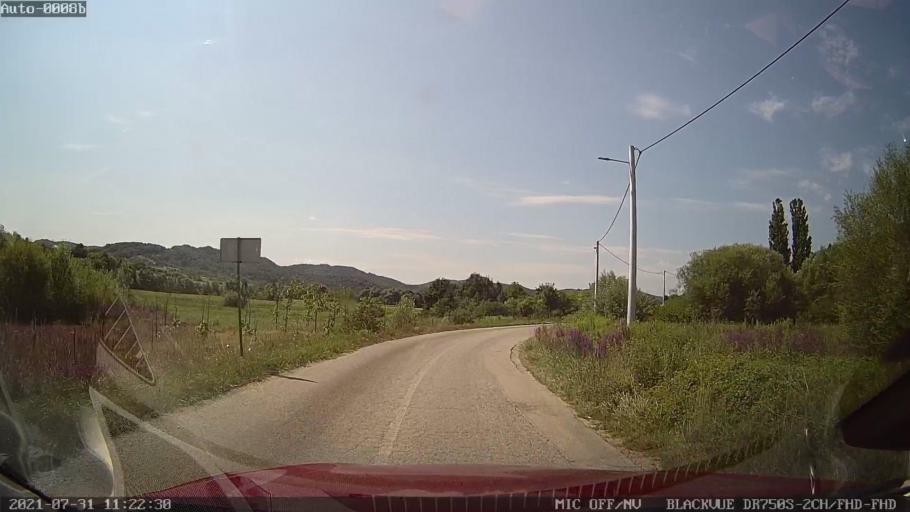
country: HR
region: Varazdinska
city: Jalzabet
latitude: 46.2218
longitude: 16.4684
